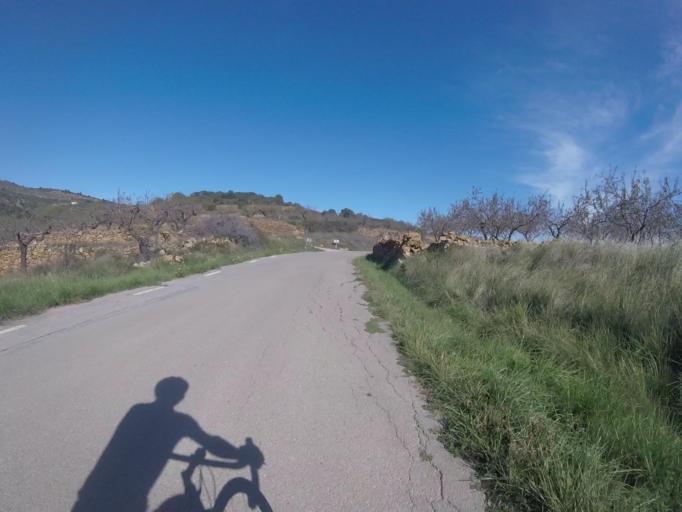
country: ES
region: Valencia
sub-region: Provincia de Castello
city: Sarratella
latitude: 40.3027
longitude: 0.0305
